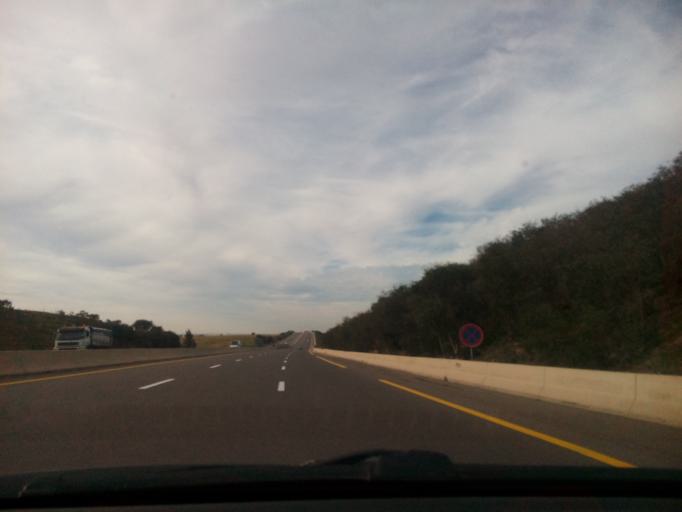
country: DZ
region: Sidi Bel Abbes
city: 'Ain el Berd
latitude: 35.3303
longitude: -0.5272
